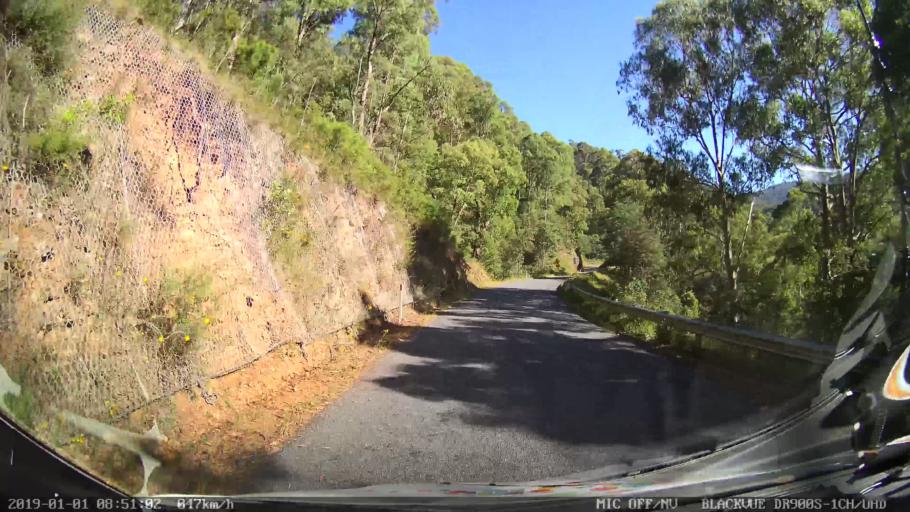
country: AU
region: New South Wales
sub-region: Snowy River
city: Jindabyne
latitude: -36.2735
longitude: 148.2001
